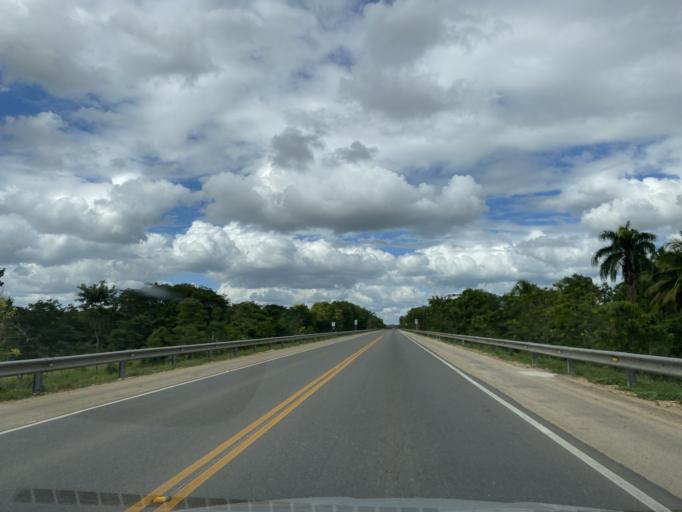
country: DO
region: Santo Domingo
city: Guerra
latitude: 18.5332
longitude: -69.7534
